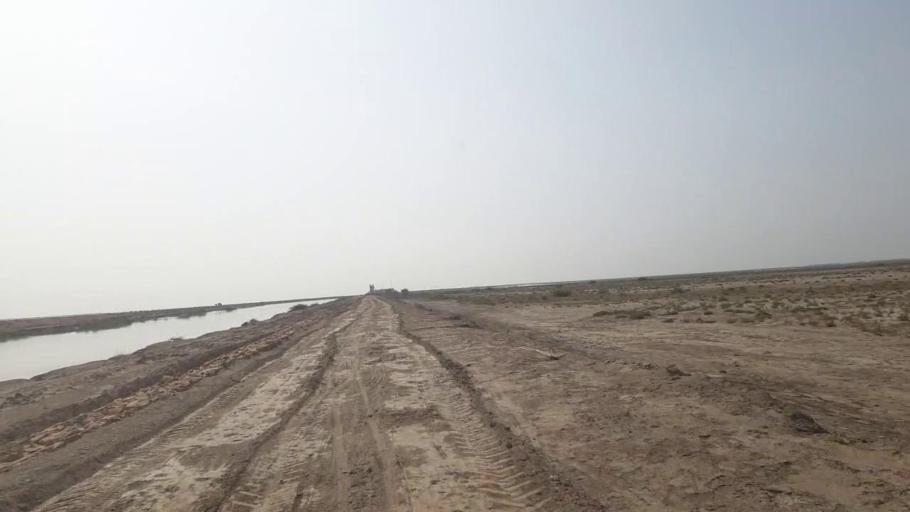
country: PK
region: Sindh
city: Kadhan
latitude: 24.3278
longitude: 68.8295
